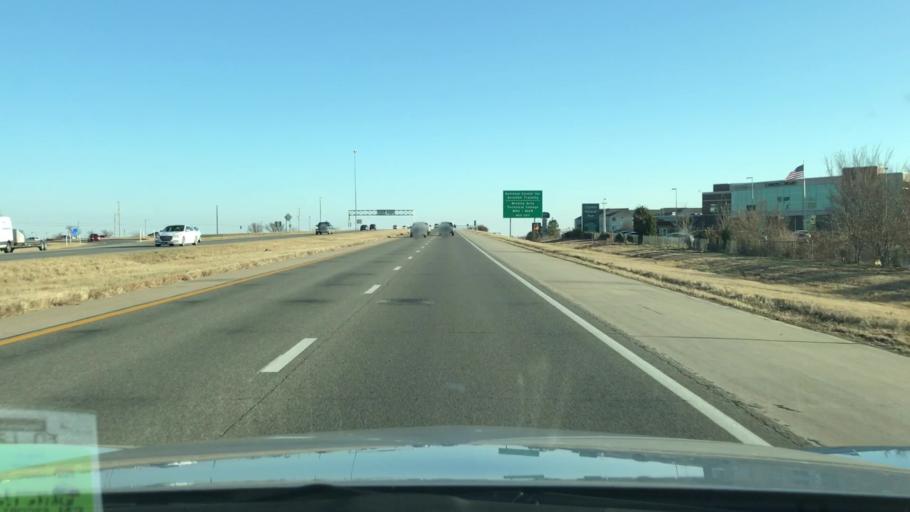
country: US
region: Kansas
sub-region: Sedgwick County
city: Bellaire
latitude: 37.7407
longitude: -97.2303
